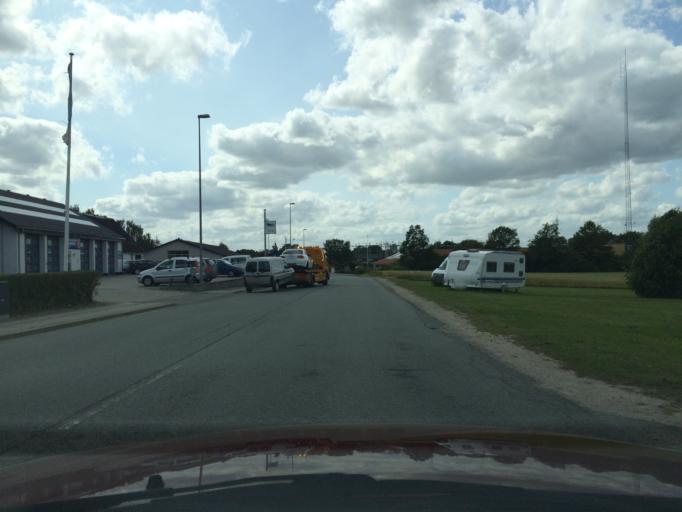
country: DK
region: Central Jutland
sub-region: Skanderborg Kommune
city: Galten
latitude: 56.1594
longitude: 9.9135
